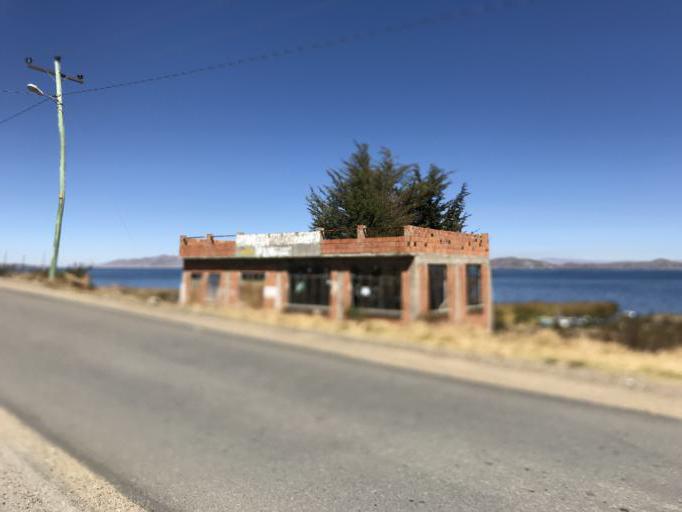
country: BO
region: La Paz
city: Huatajata
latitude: -16.2145
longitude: -68.6793
